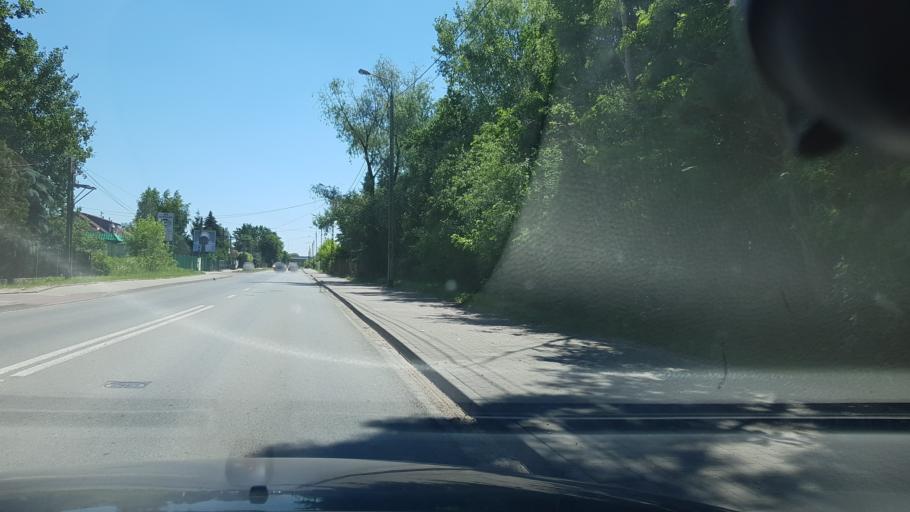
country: PL
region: Masovian Voivodeship
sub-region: Powiat wolominski
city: Marki
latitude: 52.3158
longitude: 21.1191
